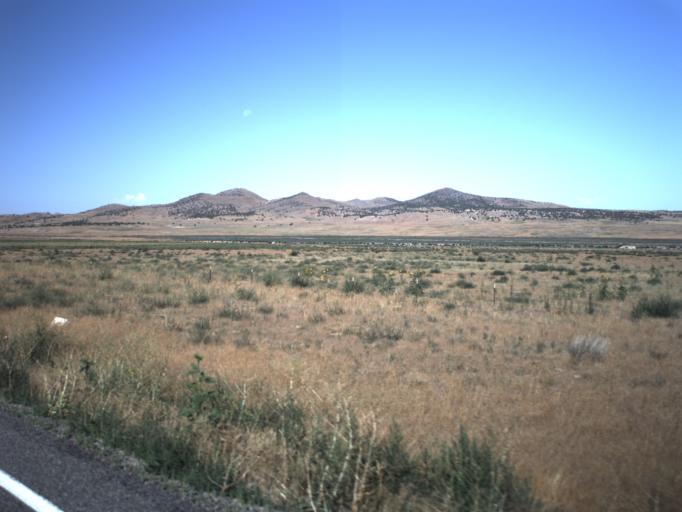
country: US
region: Utah
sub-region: Juab County
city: Nephi
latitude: 39.6897
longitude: -112.2374
